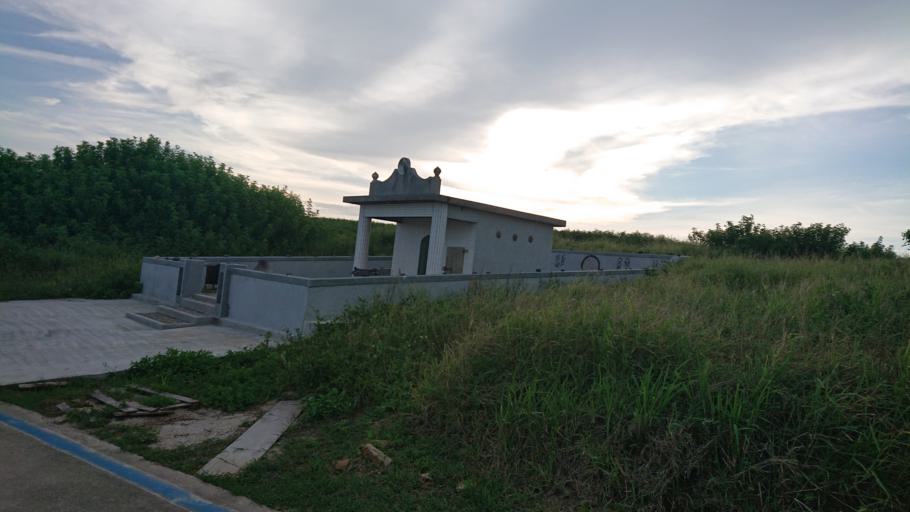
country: TW
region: Taiwan
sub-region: Penghu
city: Ma-kung
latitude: 23.5180
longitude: 119.6082
